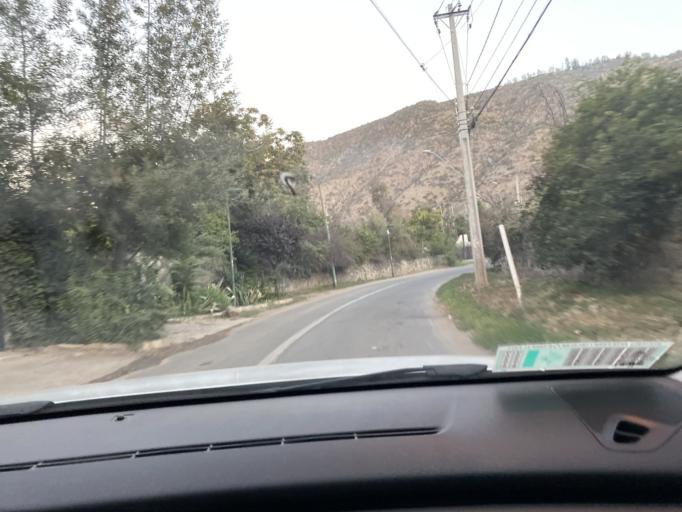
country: CL
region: Santiago Metropolitan
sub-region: Provincia de Santiago
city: Villa Presidente Frei, Nunoa, Santiago, Chile
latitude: -33.3610
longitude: -70.4829
